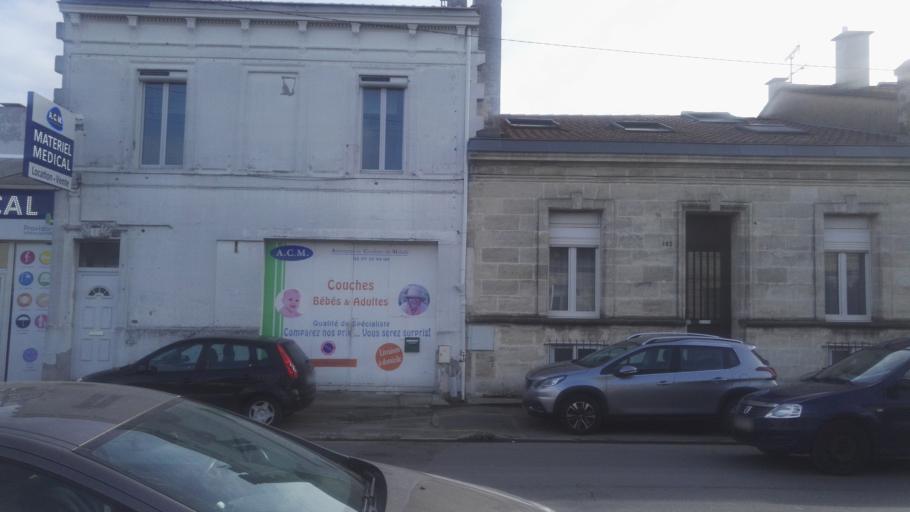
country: FR
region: Aquitaine
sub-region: Departement de la Gironde
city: Talence
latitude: 44.8064
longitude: -0.5730
